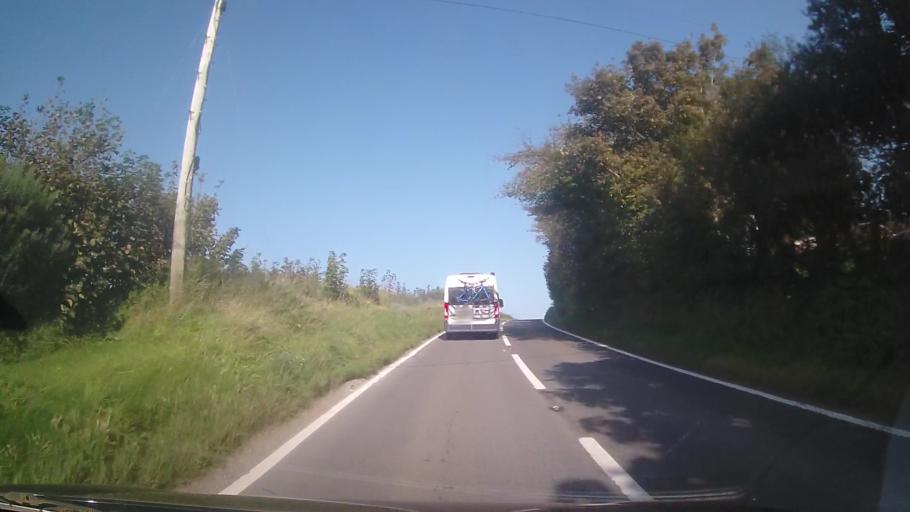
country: GB
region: Wales
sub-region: County of Ceredigion
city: Cardigan
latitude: 52.0675
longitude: -4.6794
